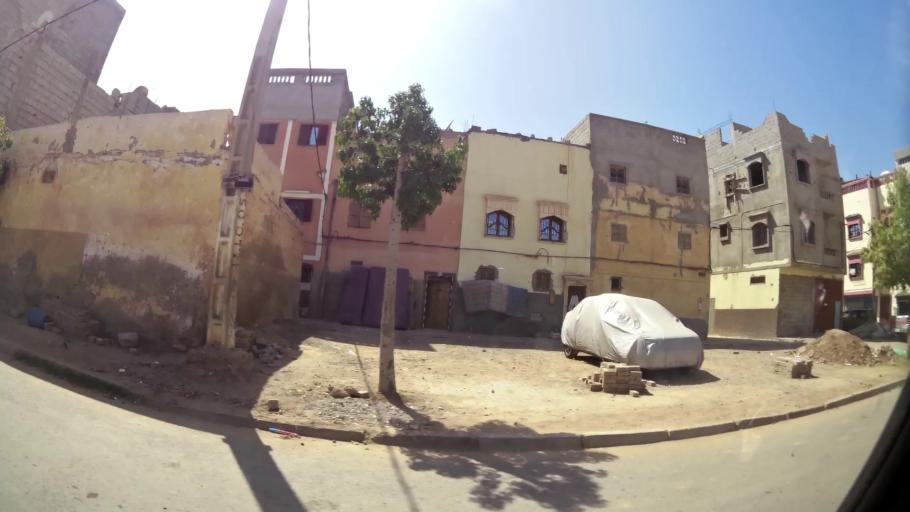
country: MA
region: Souss-Massa-Draa
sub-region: Inezgane-Ait Mellou
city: Inezgane
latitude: 30.3527
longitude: -9.5600
